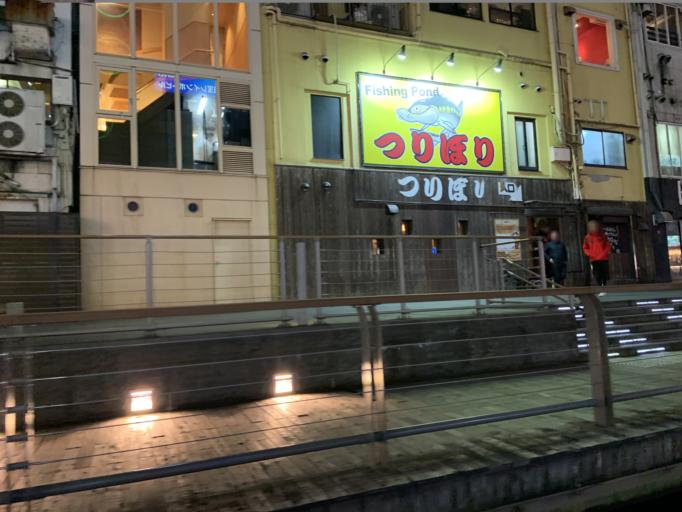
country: JP
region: Osaka
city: Osaka-shi
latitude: 34.6691
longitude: 135.5027
